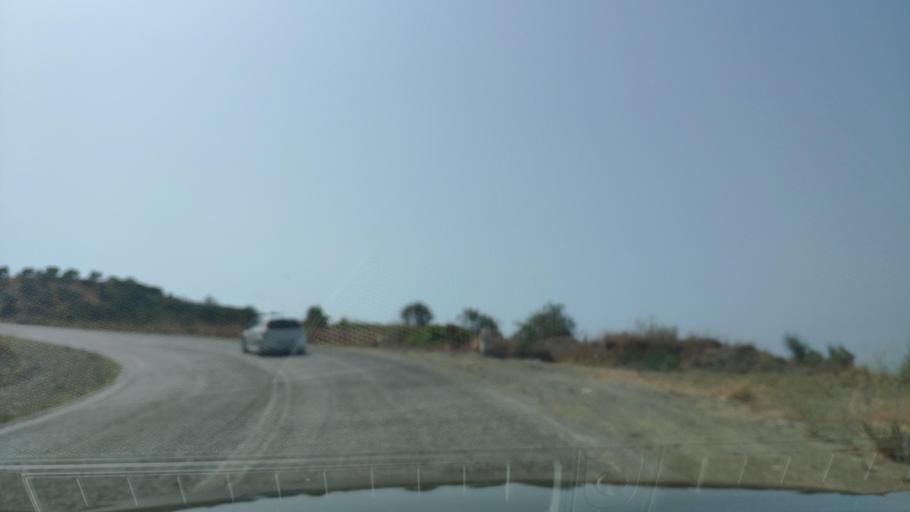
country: GR
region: Epirus
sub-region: Nomos Artas
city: Peta
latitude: 39.1685
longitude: 21.0462
